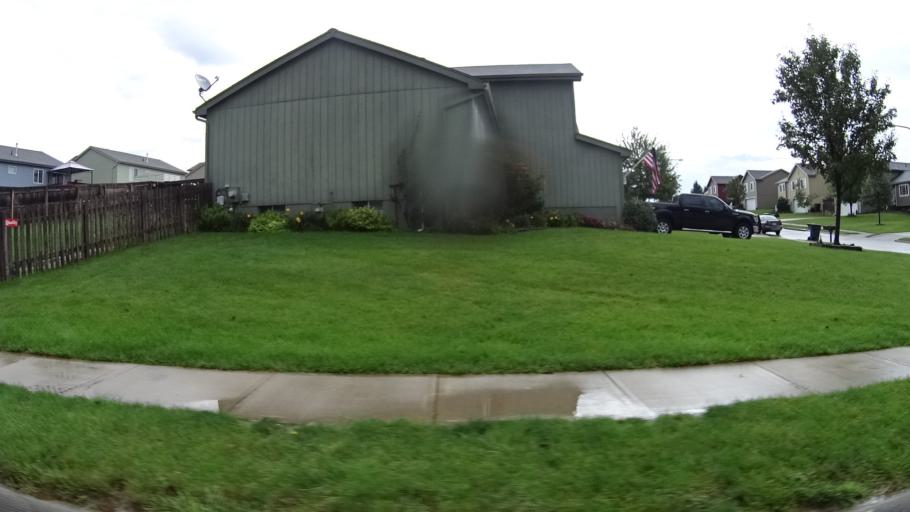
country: US
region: Nebraska
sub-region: Sarpy County
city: Offutt Air Force Base
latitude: 41.1524
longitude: -95.9503
